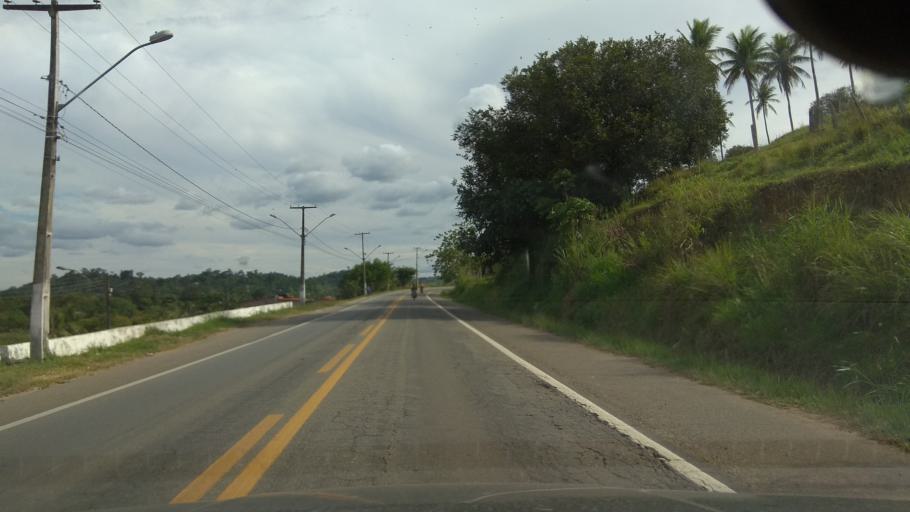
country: BR
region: Bahia
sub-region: Jitauna
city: Jitauna
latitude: -14.0151
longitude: -39.8826
